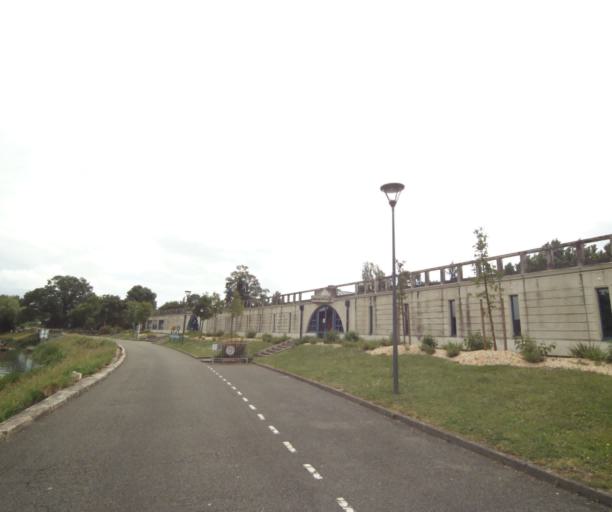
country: FR
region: Pays de la Loire
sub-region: Departement de la Sarthe
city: Sable-sur-Sarthe
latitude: 47.8367
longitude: -0.3313
